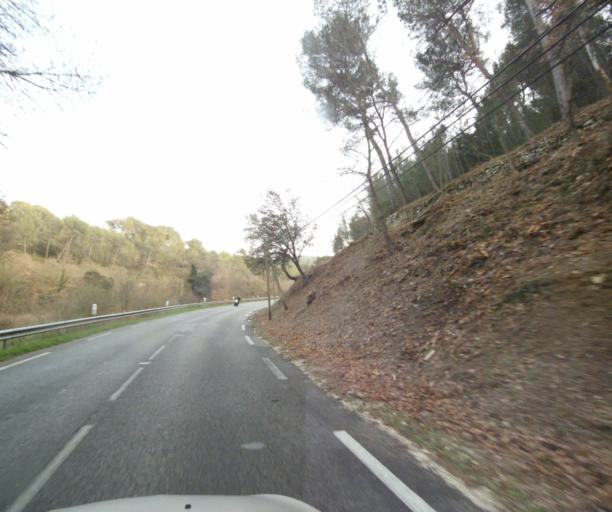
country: FR
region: Provence-Alpes-Cote d'Azur
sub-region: Departement des Bouches-du-Rhone
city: Rognes
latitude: 43.6721
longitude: 5.3521
